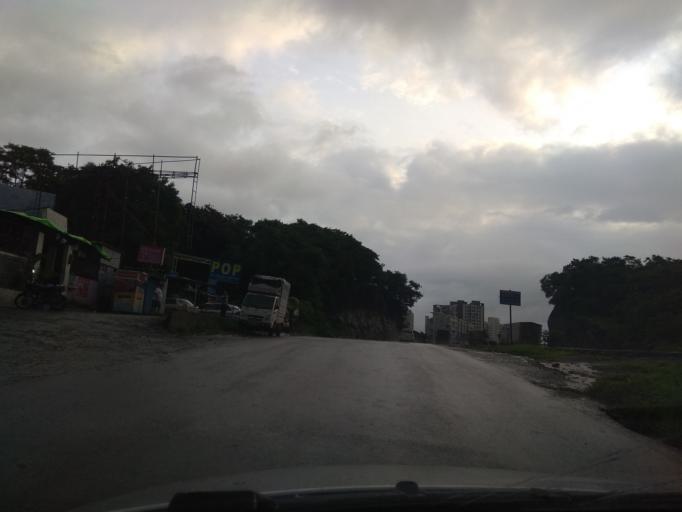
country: IN
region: Maharashtra
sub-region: Pune Division
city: Kharakvasla
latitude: 18.4958
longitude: 73.7876
